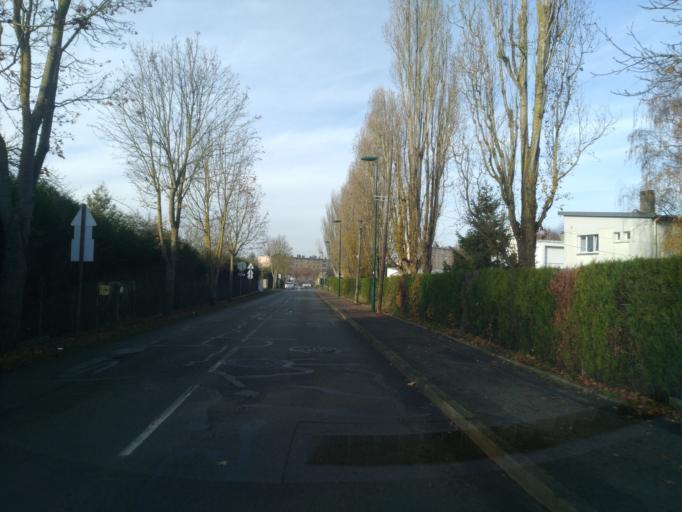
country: FR
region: Ile-de-France
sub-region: Departement des Yvelines
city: Plaisir
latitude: 48.8251
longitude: 1.9485
